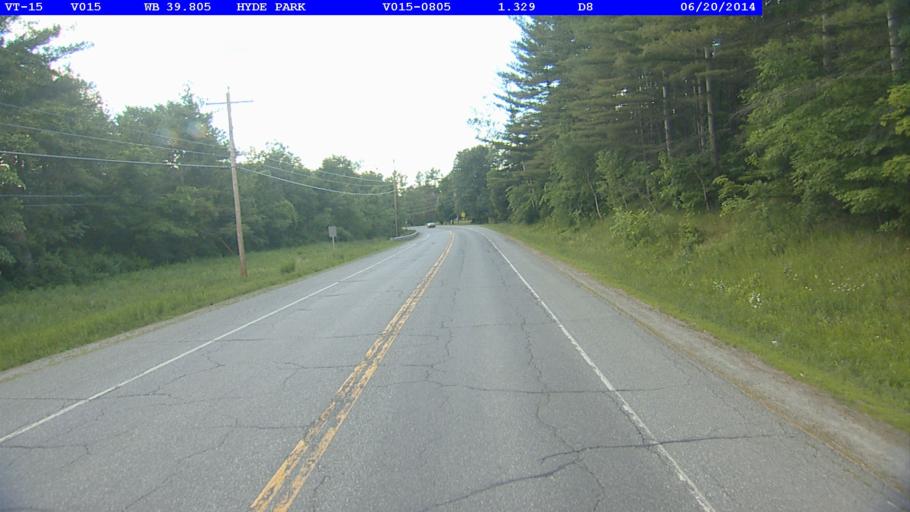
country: US
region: Vermont
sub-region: Lamoille County
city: Hyde Park
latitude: 44.5988
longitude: -72.6257
